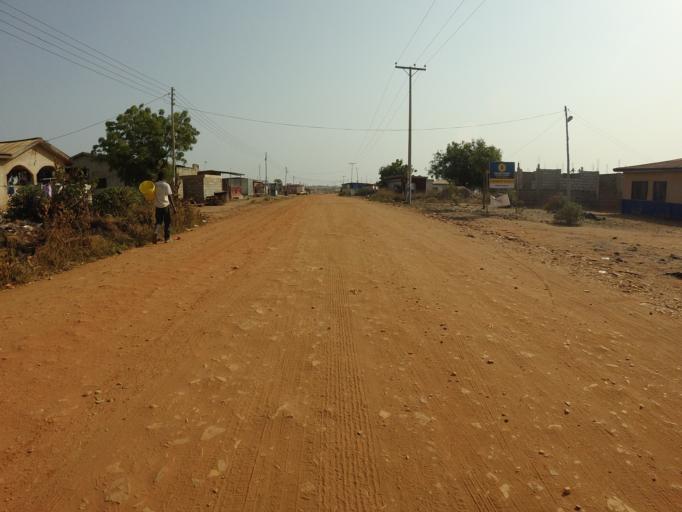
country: GH
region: Greater Accra
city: Tema
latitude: 5.7056
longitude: 0.0574
